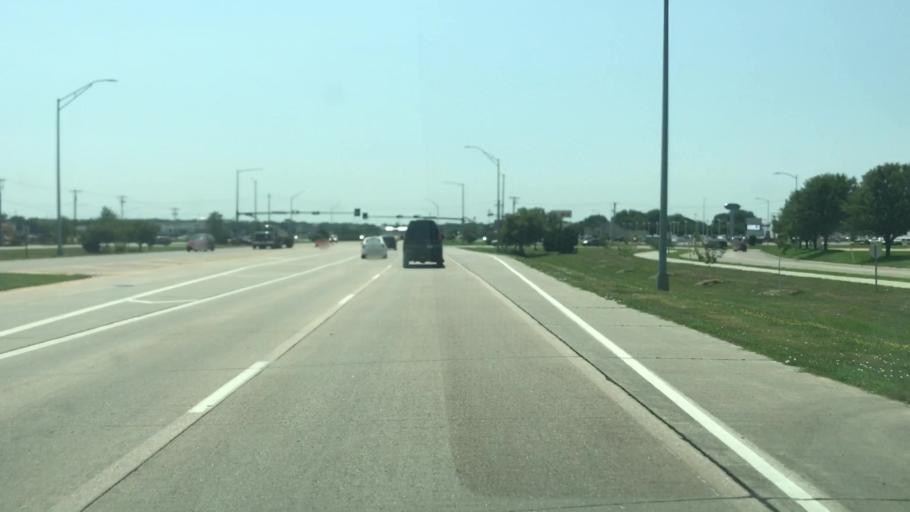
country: US
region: Nebraska
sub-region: Adams County
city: Hastings
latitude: 40.6204
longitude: -98.3831
